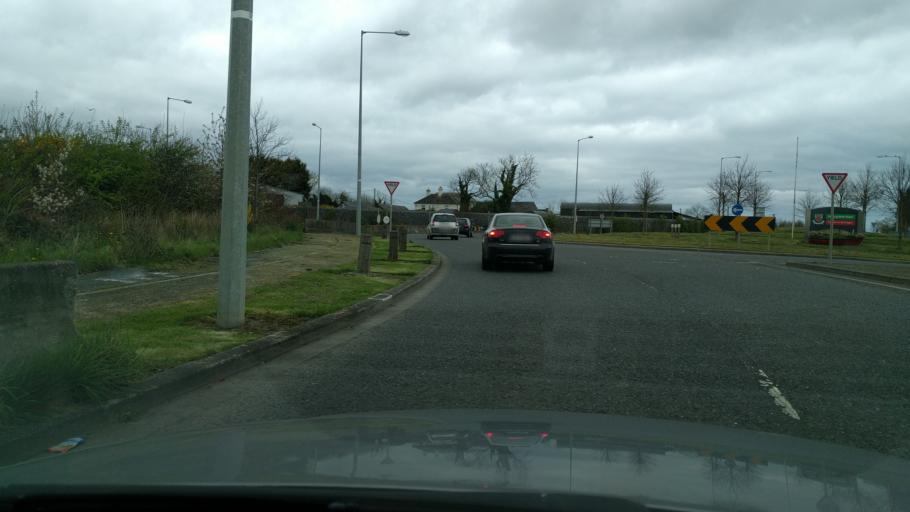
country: IE
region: Leinster
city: Balrothery
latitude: 53.6032
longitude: -6.2101
